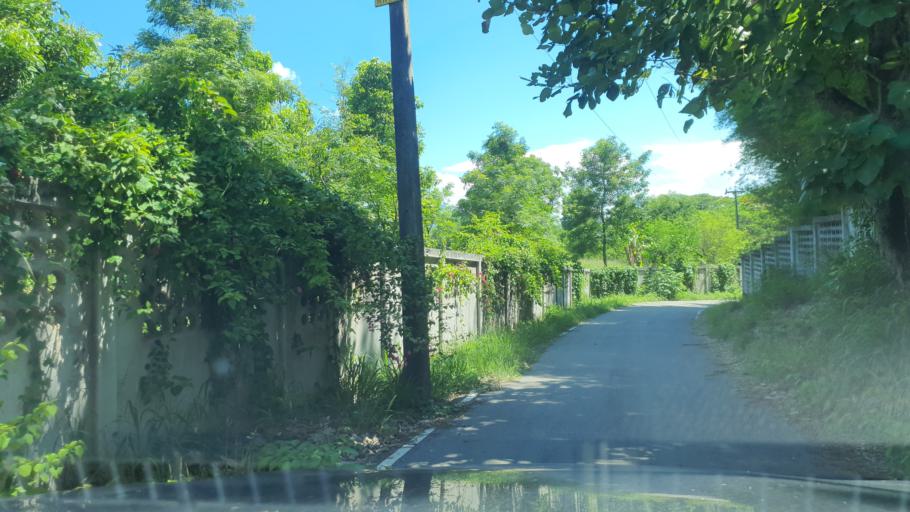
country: TH
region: Chiang Mai
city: Mae On
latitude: 18.8003
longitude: 99.2667
